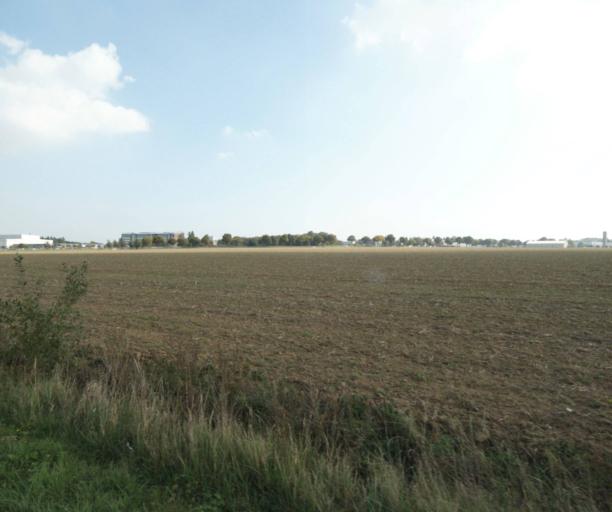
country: FR
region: Nord-Pas-de-Calais
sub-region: Departement du Nord
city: Houplin-Ancoisne
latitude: 50.5656
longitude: 3.0202
